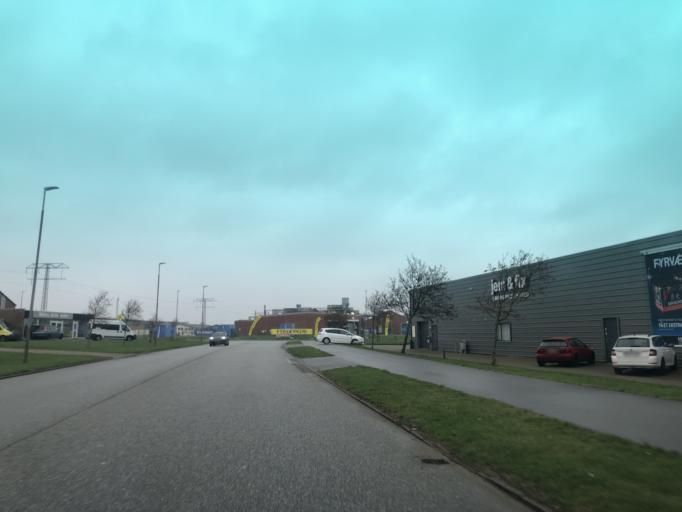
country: DK
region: Central Jutland
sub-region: Struer Kommune
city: Struer
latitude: 56.4793
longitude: 8.5811
